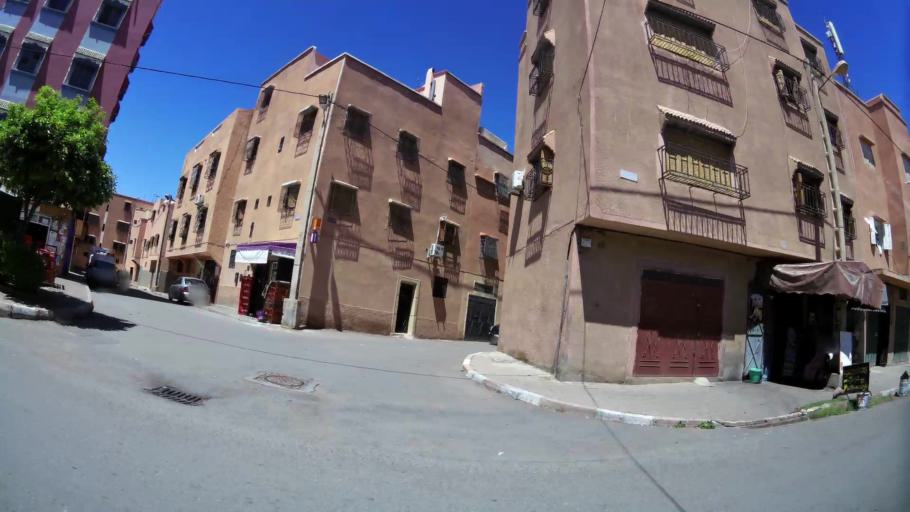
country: MA
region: Marrakech-Tensift-Al Haouz
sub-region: Marrakech
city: Marrakesh
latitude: 31.6297
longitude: -8.0512
